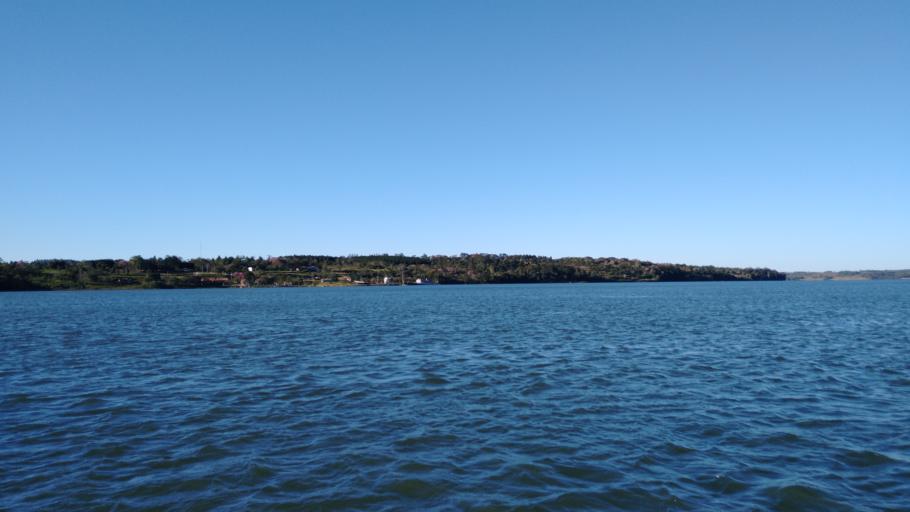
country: AR
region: Misiones
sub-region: Departamento de Candelaria
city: Candelaria
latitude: -27.4463
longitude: -55.7586
